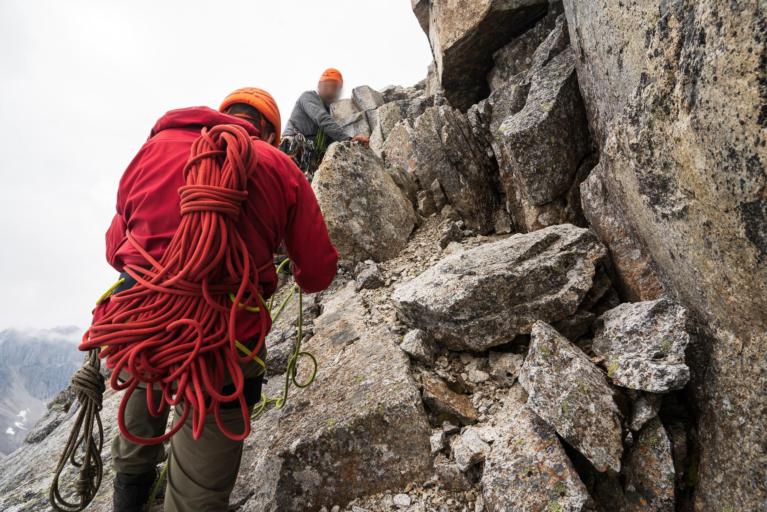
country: RU
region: Transbaikal Territory
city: Chara
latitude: 56.8655
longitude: 117.5797
